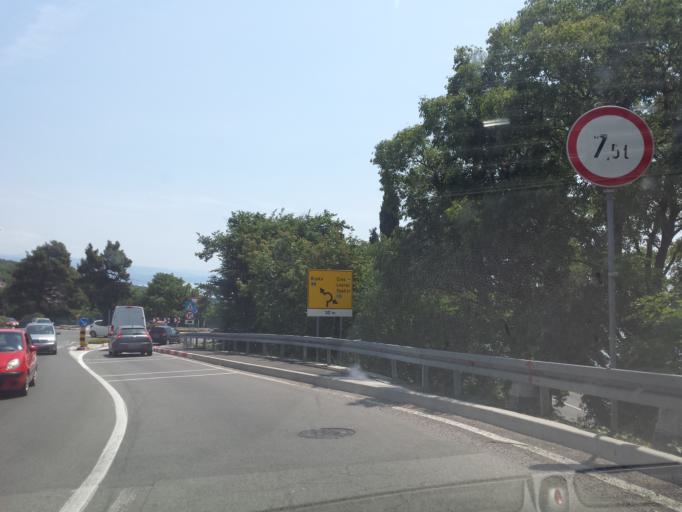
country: HR
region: Primorsko-Goranska
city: Matulji
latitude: 45.3585
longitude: 14.3288
